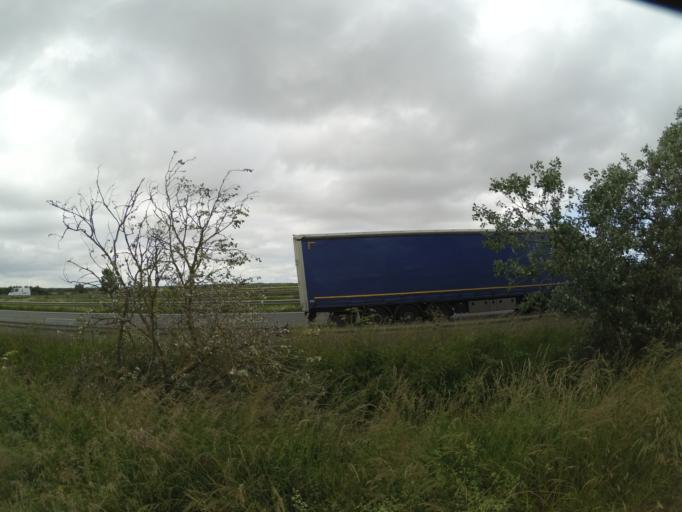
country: FR
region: Poitou-Charentes
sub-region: Departement de la Charente-Maritime
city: Yves
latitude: 46.0090
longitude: -1.0469
